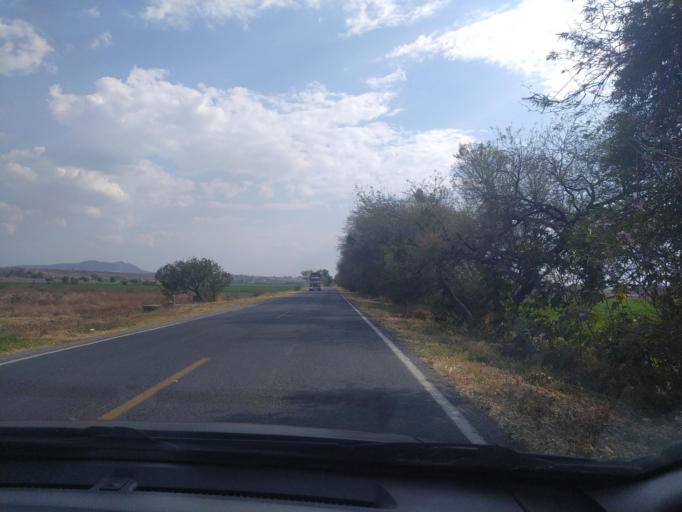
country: MX
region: Guanajuato
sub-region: San Francisco del Rincon
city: San Ignacio de Hidalgo
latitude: 20.9047
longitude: -101.8576
